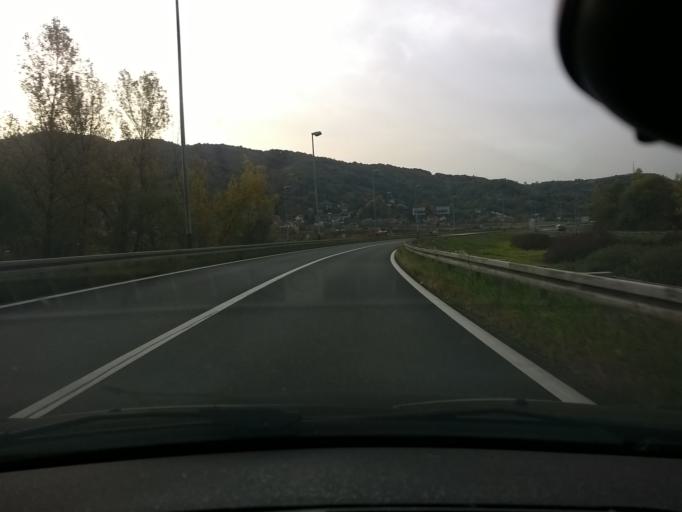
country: HR
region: Zagrebacka
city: Zapresic
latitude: 45.8515
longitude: 15.8293
